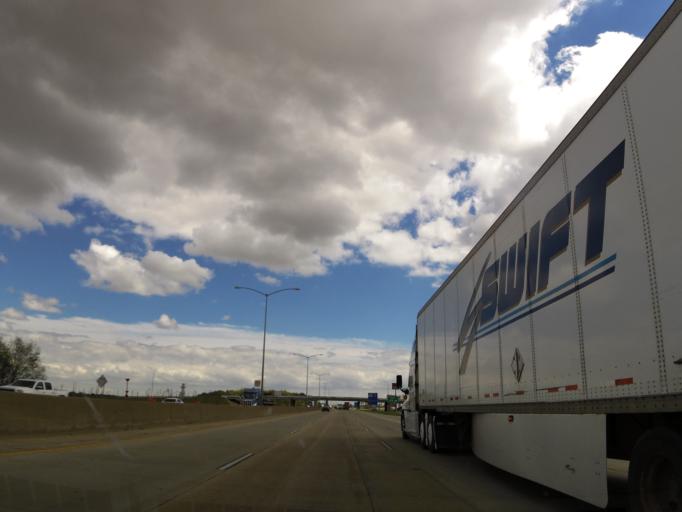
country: US
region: Arkansas
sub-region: Crittenden County
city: West Memphis
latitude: 35.1662
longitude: -90.1791
